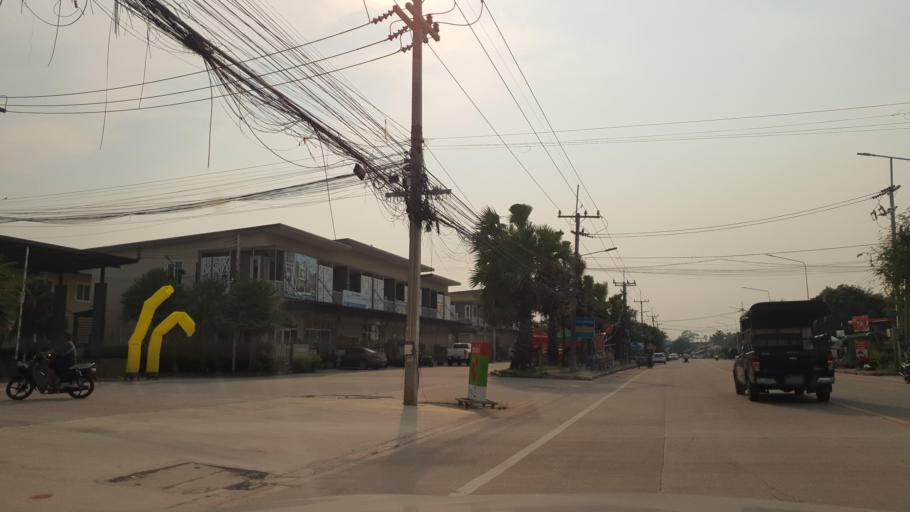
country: TH
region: Rayong
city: Rayong
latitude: 12.6190
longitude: 101.4069
